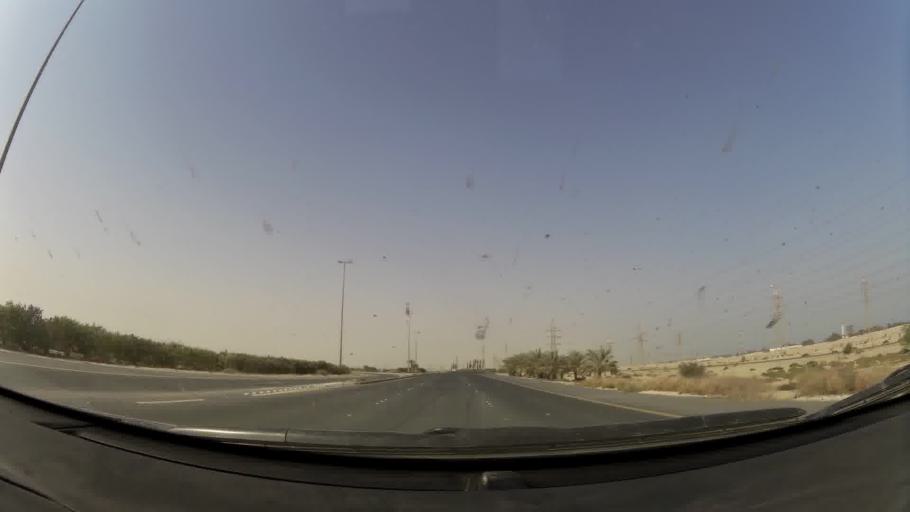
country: KW
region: Al Ahmadi
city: Al Fahahil
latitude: 28.9306
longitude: 48.1970
